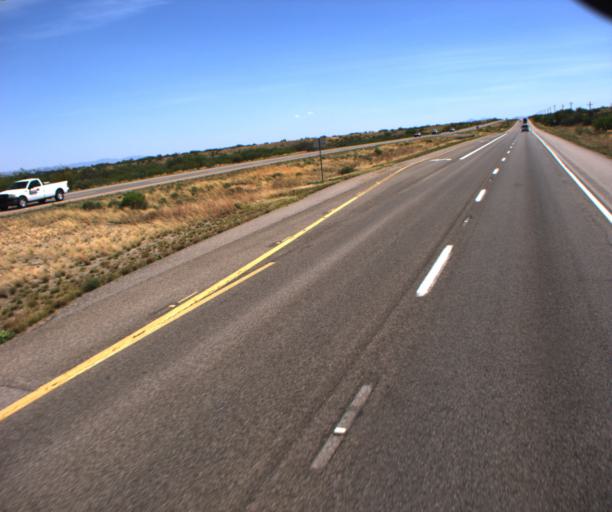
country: US
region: Arizona
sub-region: Cochise County
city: Whetstone
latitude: 31.9030
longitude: -110.3414
